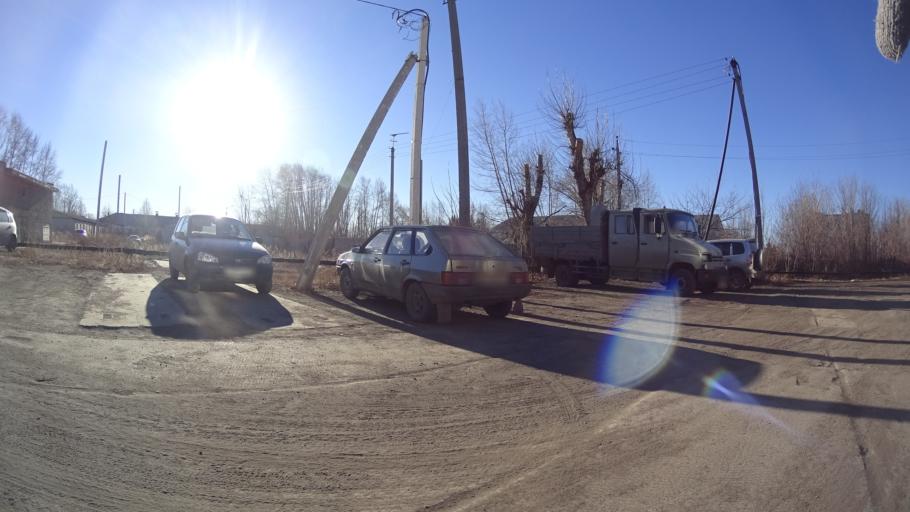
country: RU
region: Chelyabinsk
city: Troitsk
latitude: 54.1095
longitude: 61.5532
